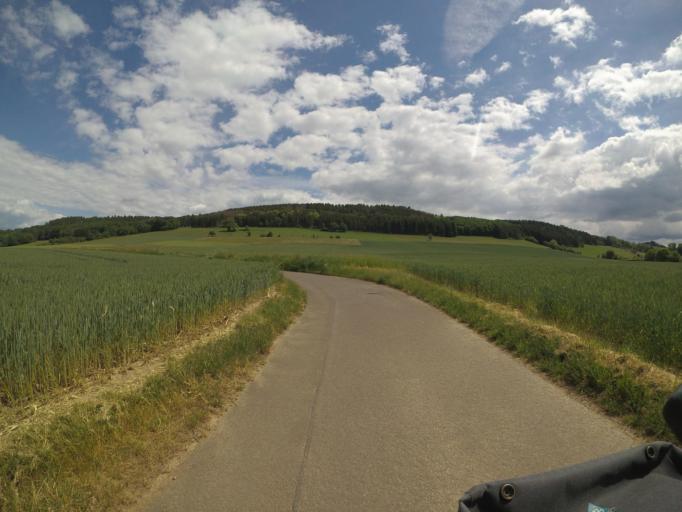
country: DE
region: Rheinland-Pfalz
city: Wiesweiler
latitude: 49.6406
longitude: 7.5750
